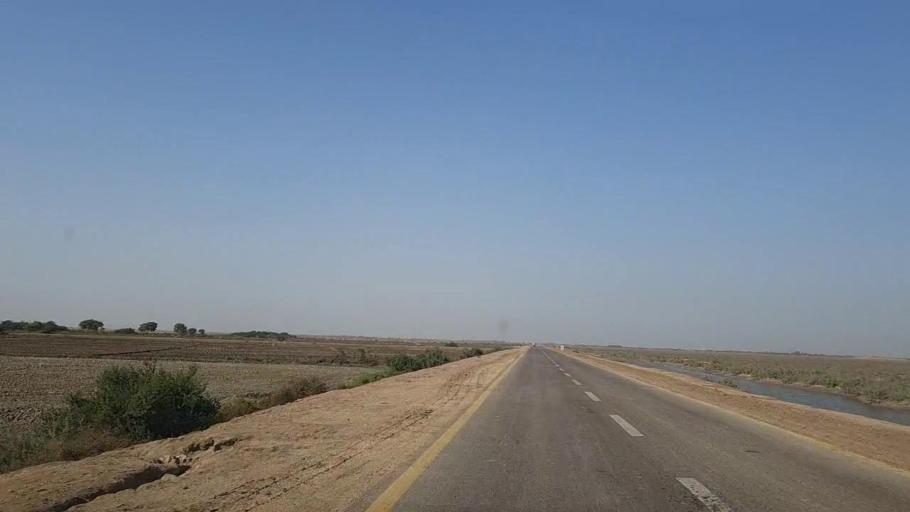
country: PK
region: Sindh
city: Jati
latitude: 24.4843
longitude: 68.3739
